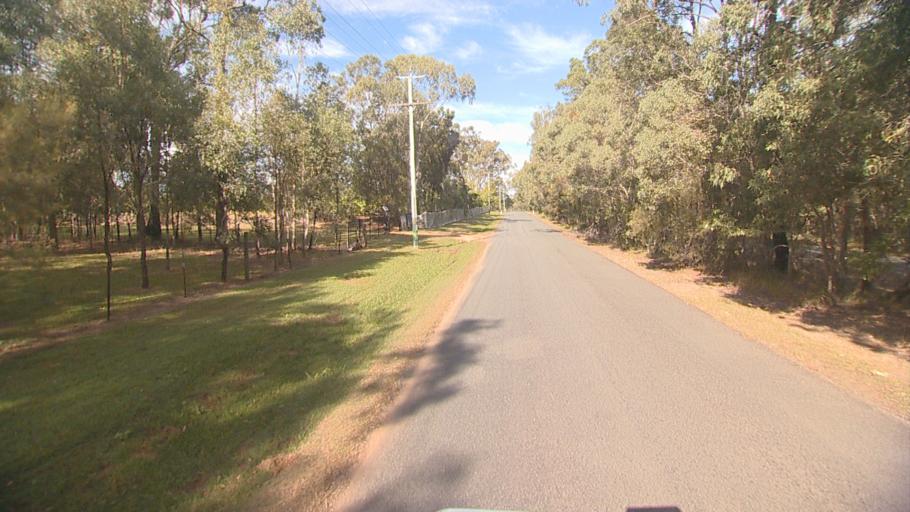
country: AU
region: Queensland
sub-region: Brisbane
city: Forest Lake
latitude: -27.6549
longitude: 152.9830
